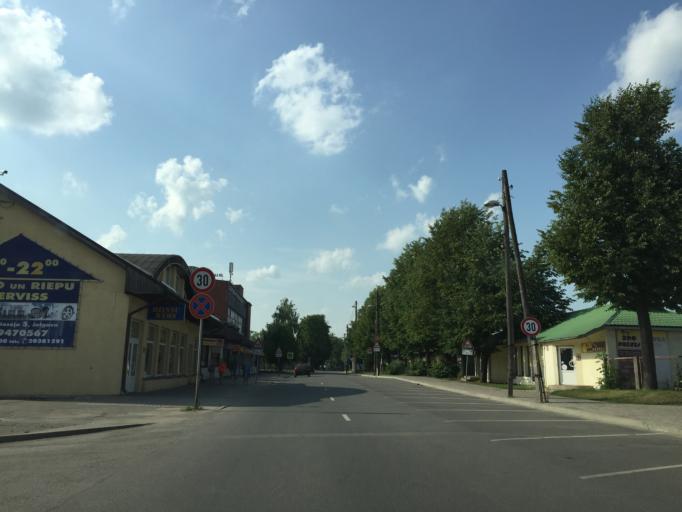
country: LV
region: Jelgava
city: Jelgava
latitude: 56.6564
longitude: 23.7217
